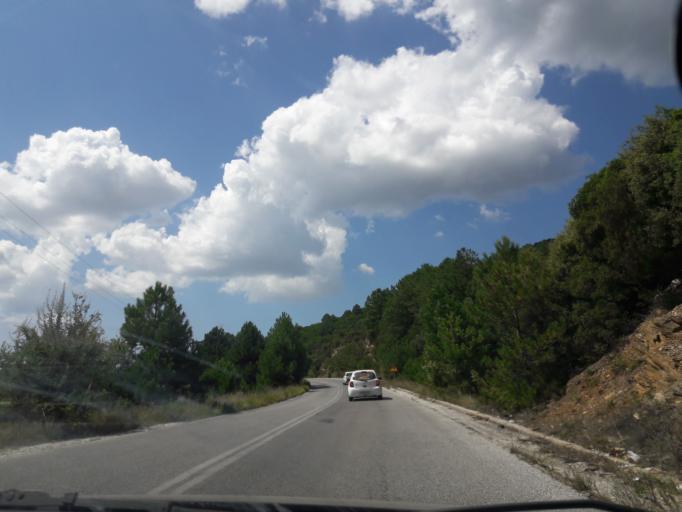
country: GR
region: Central Macedonia
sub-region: Nomos Chalkidikis
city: Polygyros
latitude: 40.3577
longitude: 23.4943
